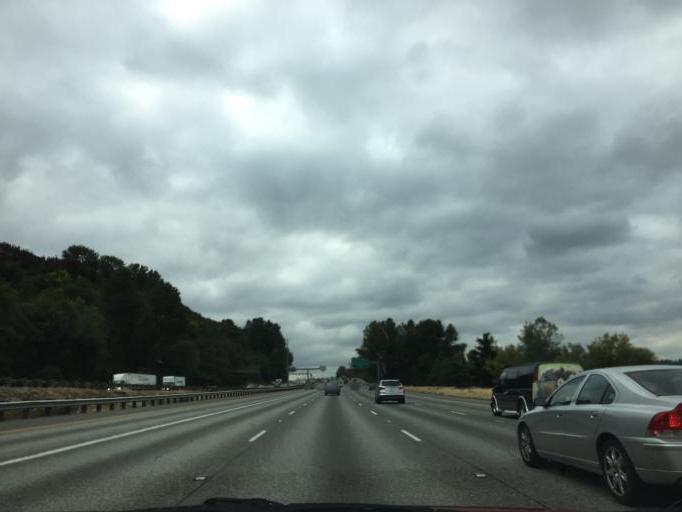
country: US
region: Washington
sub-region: King County
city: Riverton
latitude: 47.5254
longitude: -122.2922
